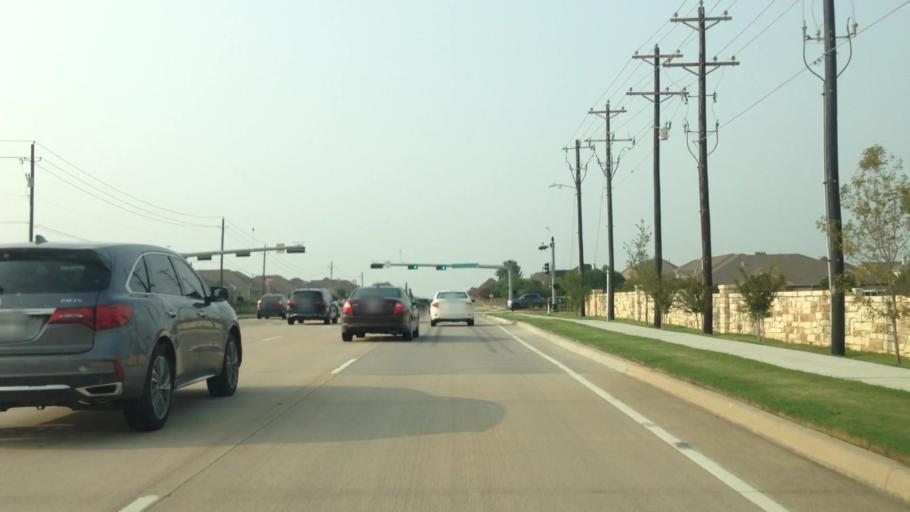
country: US
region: Texas
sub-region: Denton County
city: The Colony
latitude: 33.0344
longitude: -96.9184
